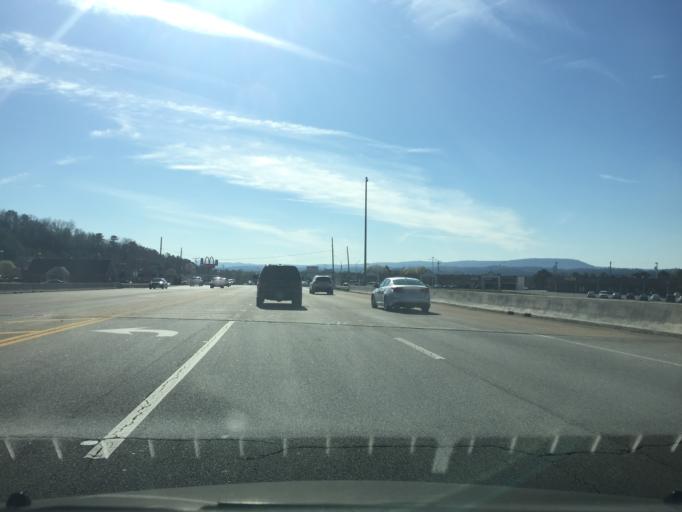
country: US
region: Tennessee
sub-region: Hamilton County
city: East Brainerd
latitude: 35.0326
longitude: -85.1820
